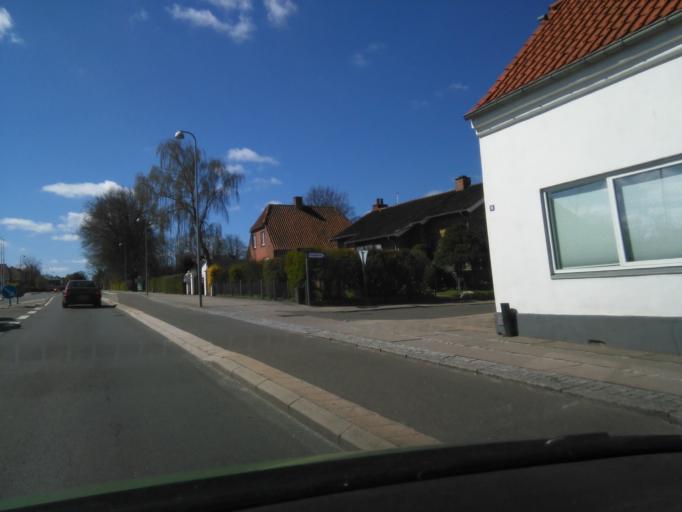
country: DK
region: Central Jutland
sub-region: Horsens Kommune
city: Horsens
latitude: 55.8506
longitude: 9.8290
